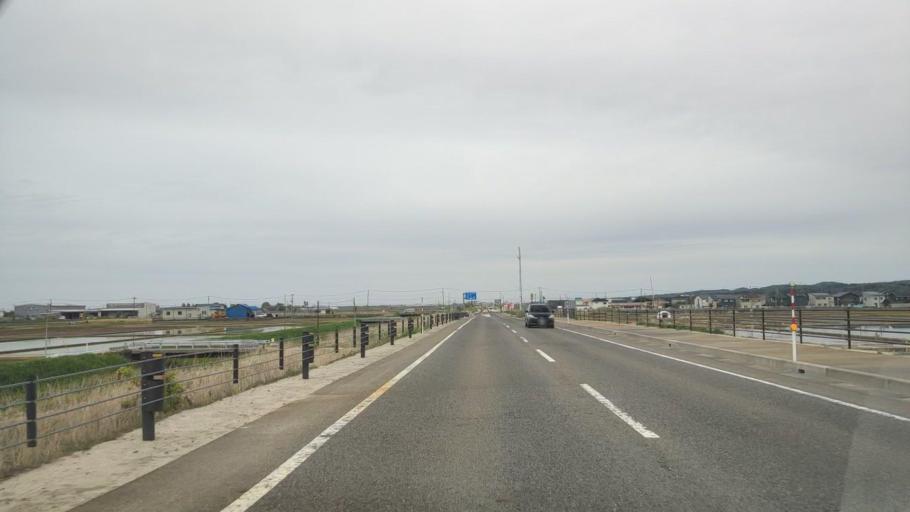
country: JP
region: Niigata
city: Niitsu-honcho
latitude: 37.7482
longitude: 139.0855
